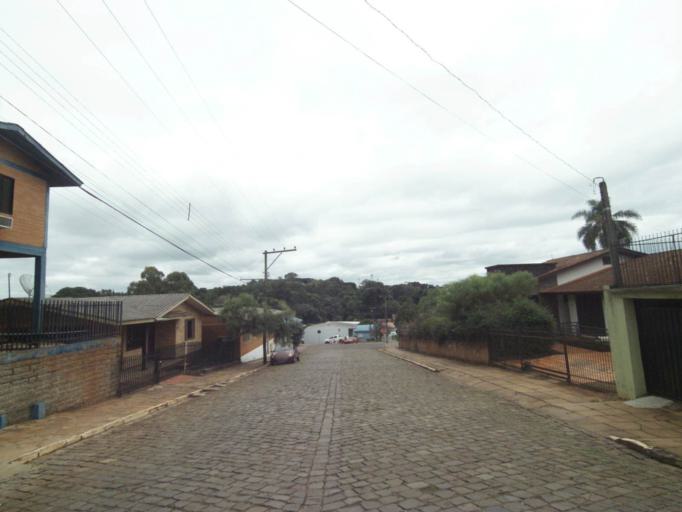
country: BR
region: Rio Grande do Sul
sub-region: Lagoa Vermelha
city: Lagoa Vermelha
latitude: -28.2079
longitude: -51.5291
